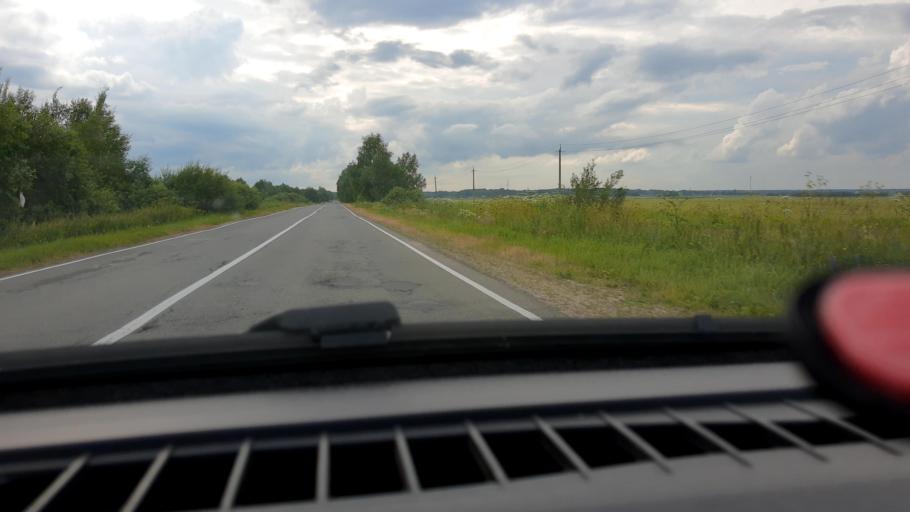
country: RU
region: Nizjnij Novgorod
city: Neklyudovo
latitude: 56.5243
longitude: 43.8658
